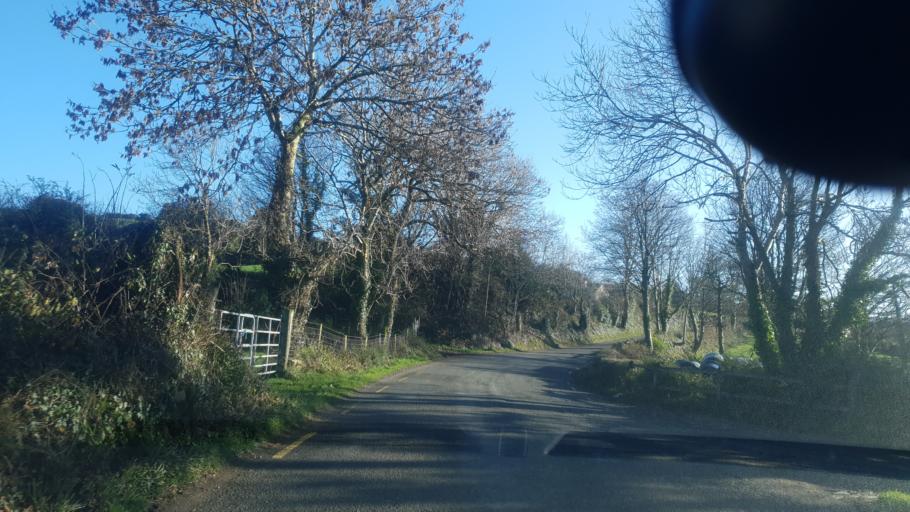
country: IE
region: Munster
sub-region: Ciarrai
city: Cill Airne
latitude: 52.1099
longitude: -9.4977
